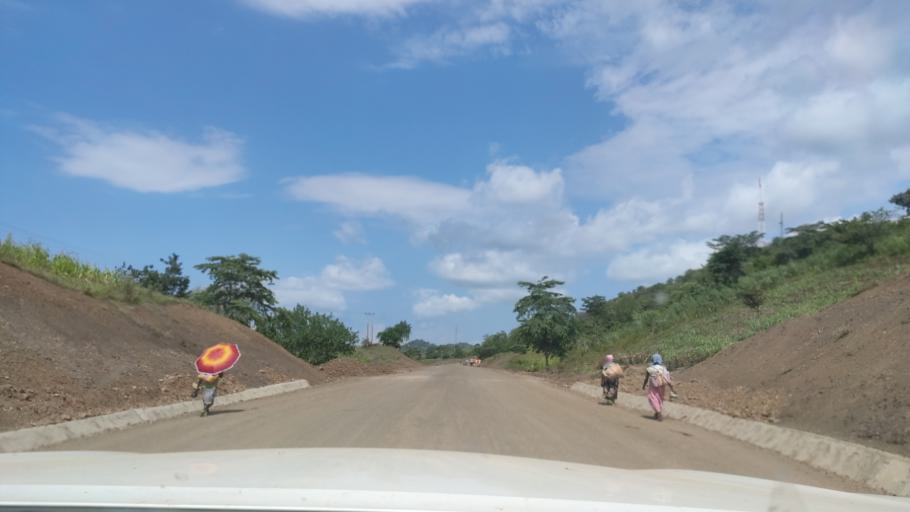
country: ET
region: Southern Nations, Nationalities, and People's Region
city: Felege Neway
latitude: 6.3919
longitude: 37.0694
